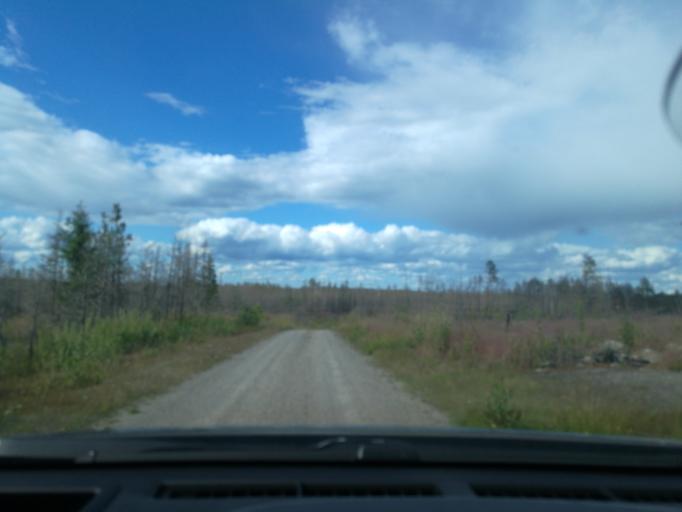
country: SE
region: Vaestmanland
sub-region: Surahammars Kommun
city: Ramnas
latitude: 59.8440
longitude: 16.2473
